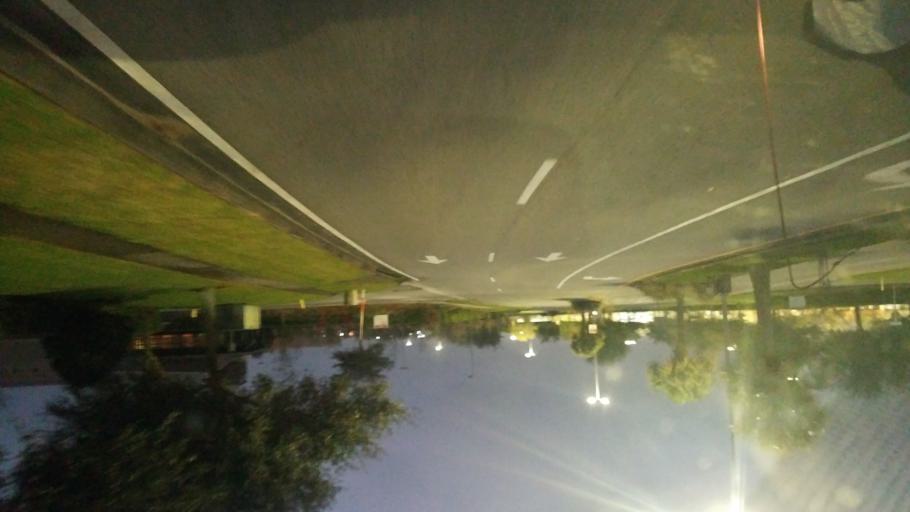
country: US
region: Florida
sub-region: Polk County
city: Citrus Ridge
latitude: 28.3464
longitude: -81.6128
